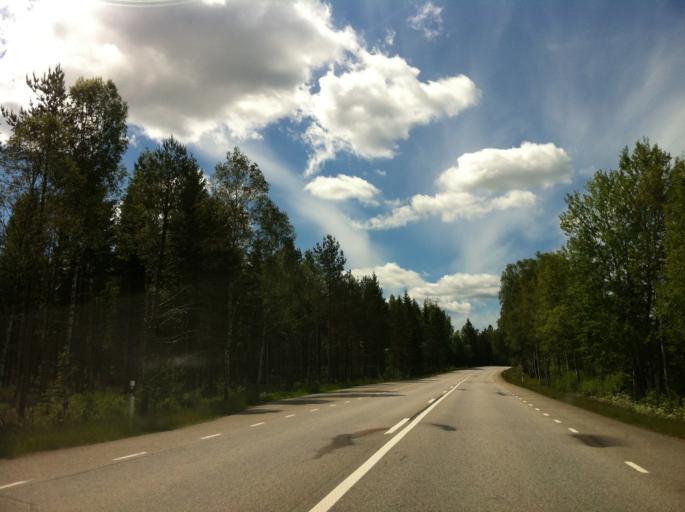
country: SE
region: Vaestra Goetaland
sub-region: Amals Kommun
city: Amal
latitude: 58.9929
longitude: 12.6736
